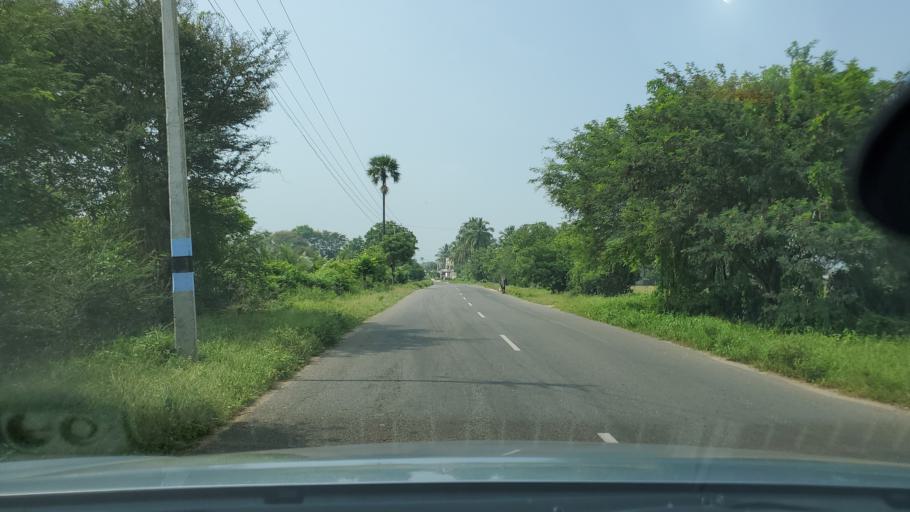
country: IN
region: Tamil Nadu
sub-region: Erode
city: Chennimalai
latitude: 11.1972
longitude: 77.6274
